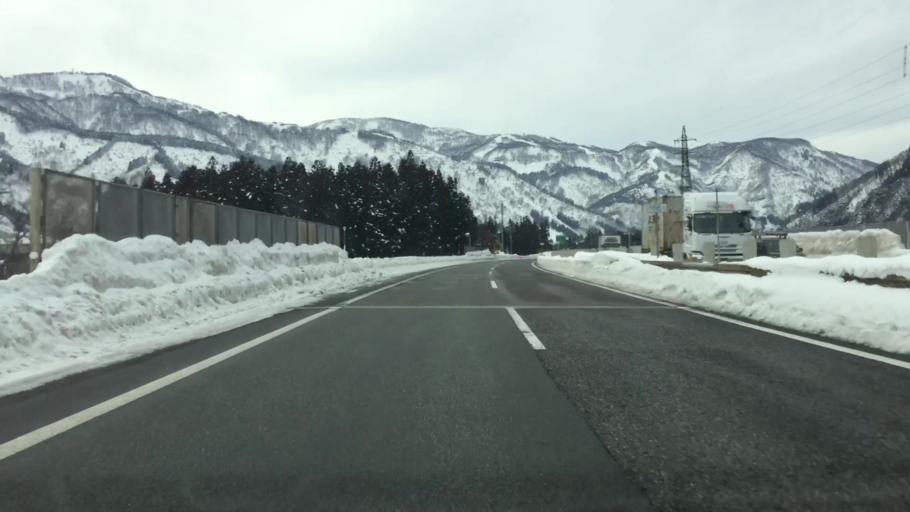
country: JP
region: Niigata
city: Shiozawa
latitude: 36.9299
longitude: 138.8348
